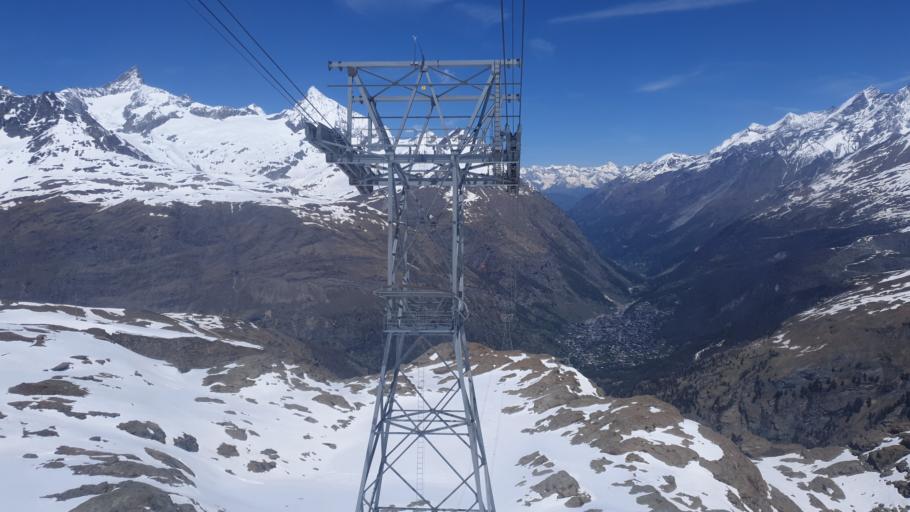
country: CH
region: Valais
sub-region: Visp District
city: Zermatt
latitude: 45.9766
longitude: 7.7240
